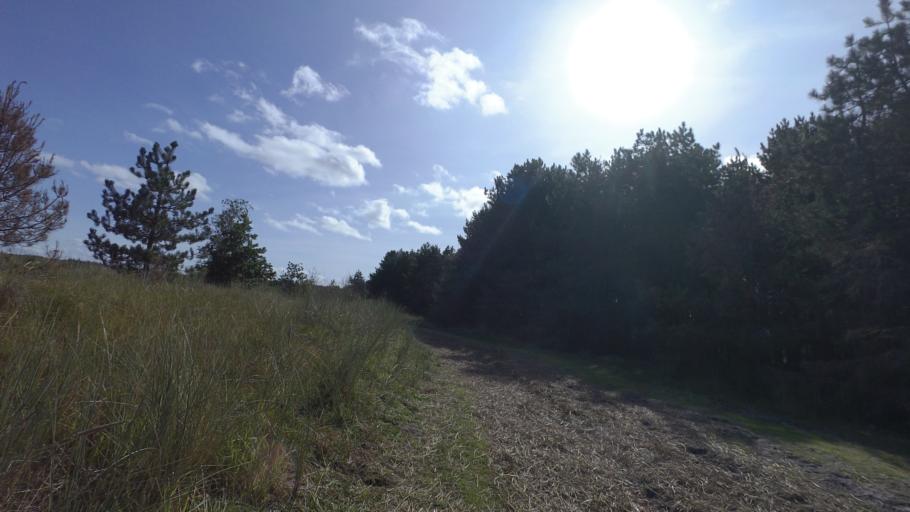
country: NL
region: Friesland
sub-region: Gemeente Ameland
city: Hollum
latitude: 53.4529
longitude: 5.6962
